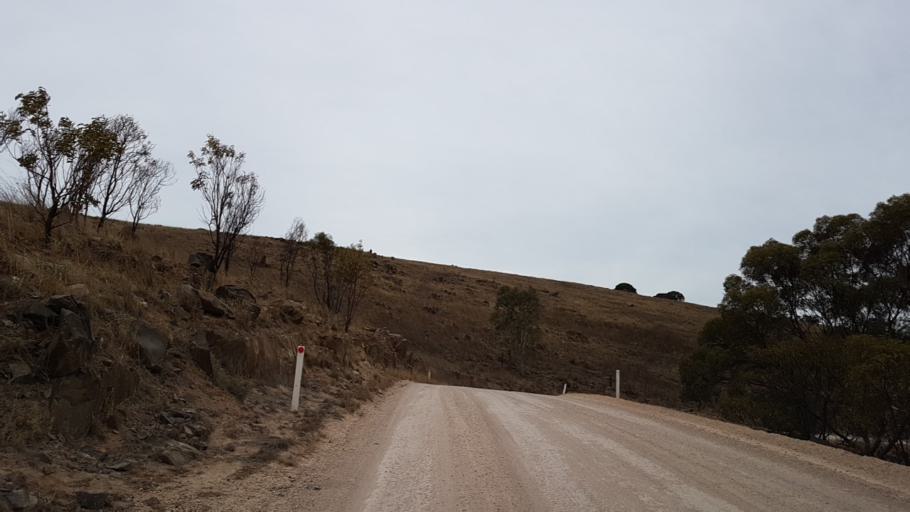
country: AU
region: South Australia
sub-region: Mount Barker
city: Callington
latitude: -35.0030
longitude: 139.0271
